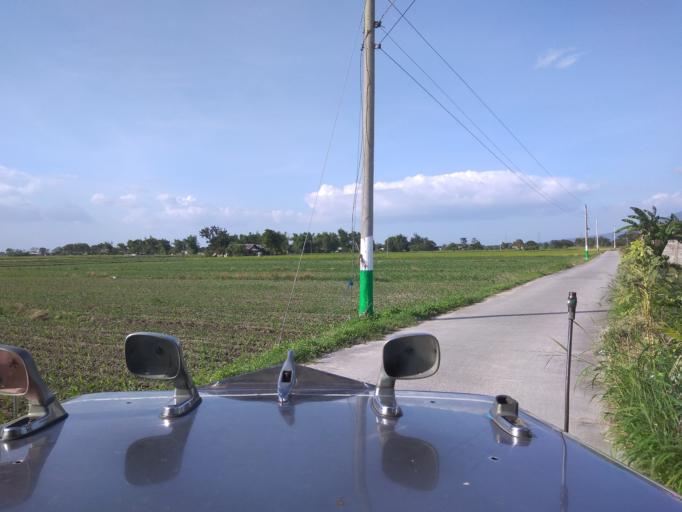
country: PH
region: Central Luzon
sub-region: Province of Pampanga
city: Bulaon
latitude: 15.0965
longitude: 120.6938
